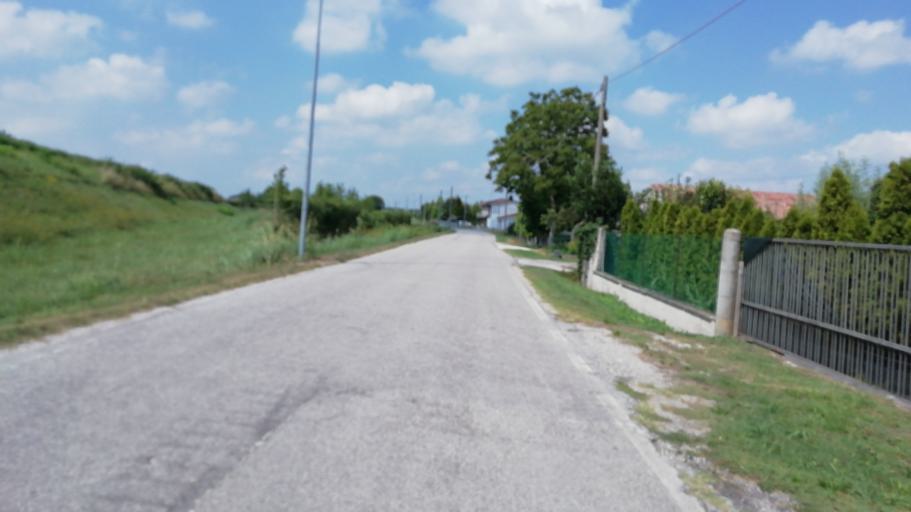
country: IT
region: Veneto
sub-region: Provincia di Rovigo
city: Gaiba
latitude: 44.9456
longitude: 11.5009
